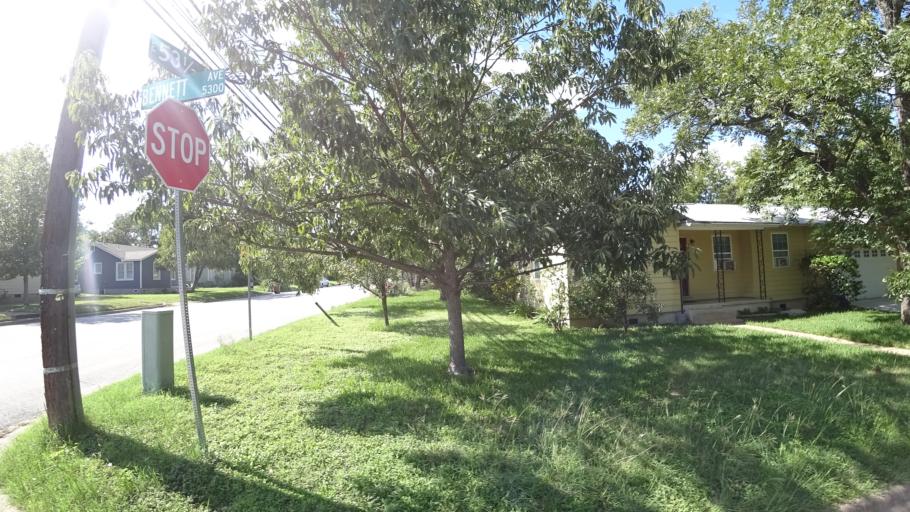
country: US
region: Texas
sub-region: Travis County
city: Austin
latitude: 30.3138
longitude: -97.7118
